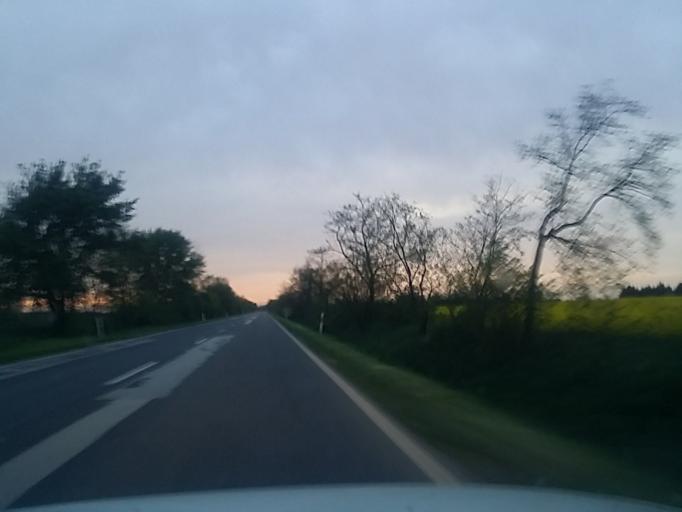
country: HU
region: Bekes
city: Csorvas
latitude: 46.7199
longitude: 20.9307
